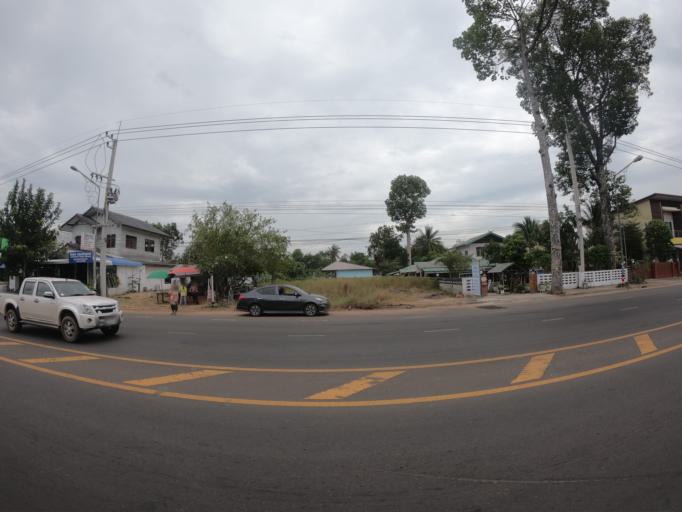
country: TH
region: Roi Et
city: Chiang Khwan
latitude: 16.1103
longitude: 103.8403
